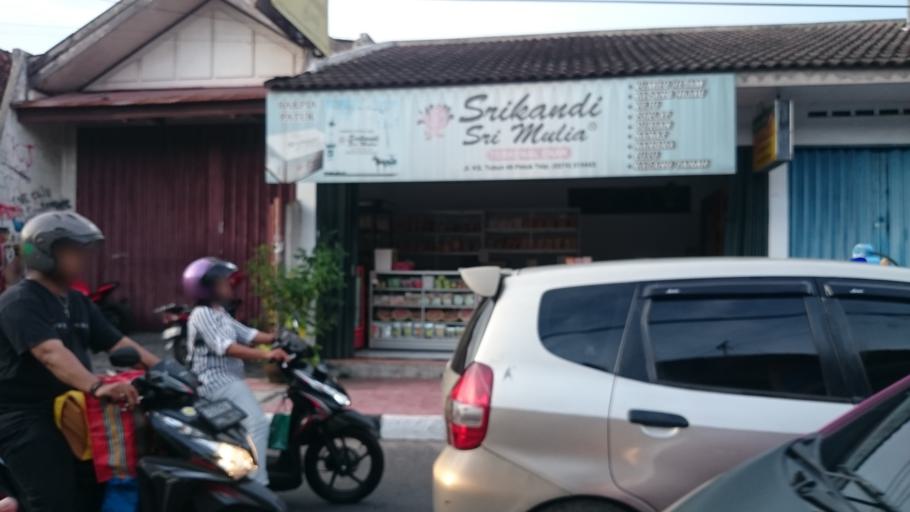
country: ID
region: Daerah Istimewa Yogyakarta
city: Yogyakarta
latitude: -7.7975
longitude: 110.3584
